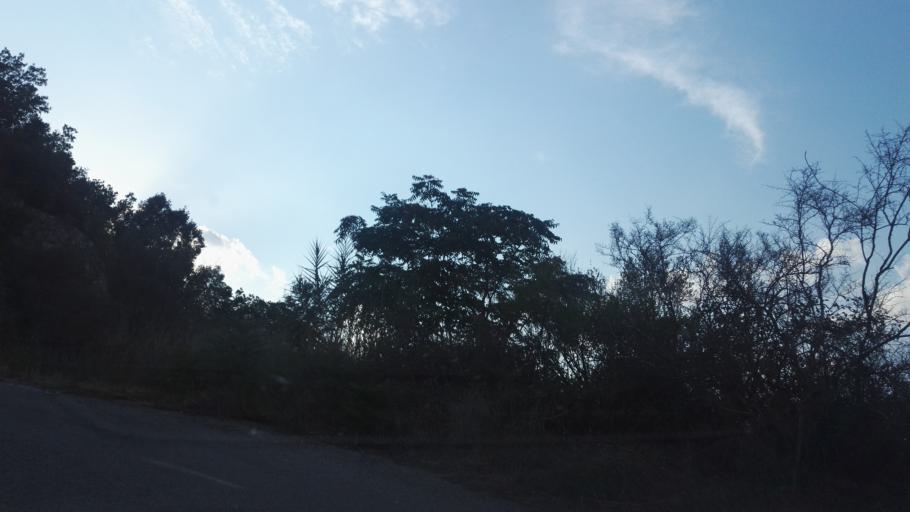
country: IT
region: Calabria
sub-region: Provincia di Reggio Calabria
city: Camini
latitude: 38.4348
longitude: 16.4798
